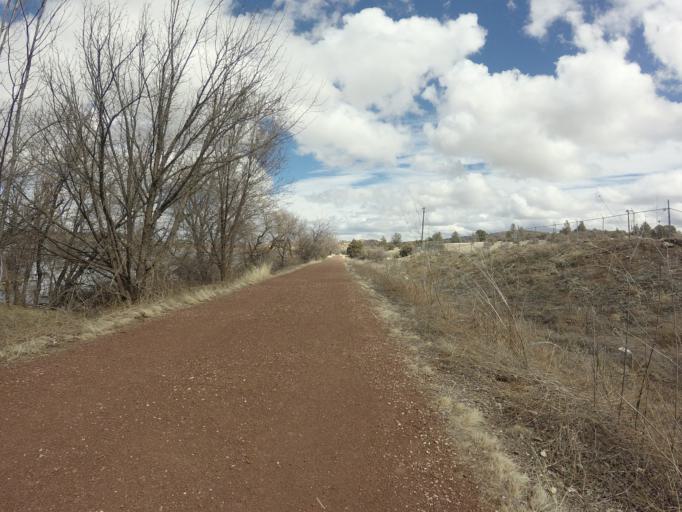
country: US
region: Arizona
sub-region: Yavapai County
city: Prescott
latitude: 34.5810
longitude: -112.4237
